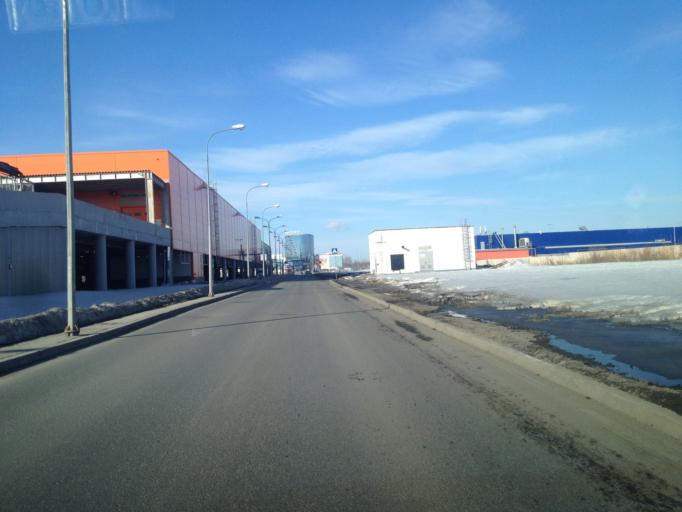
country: RU
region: Sverdlovsk
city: Shirokaya Rechka
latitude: 56.8222
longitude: 60.5093
